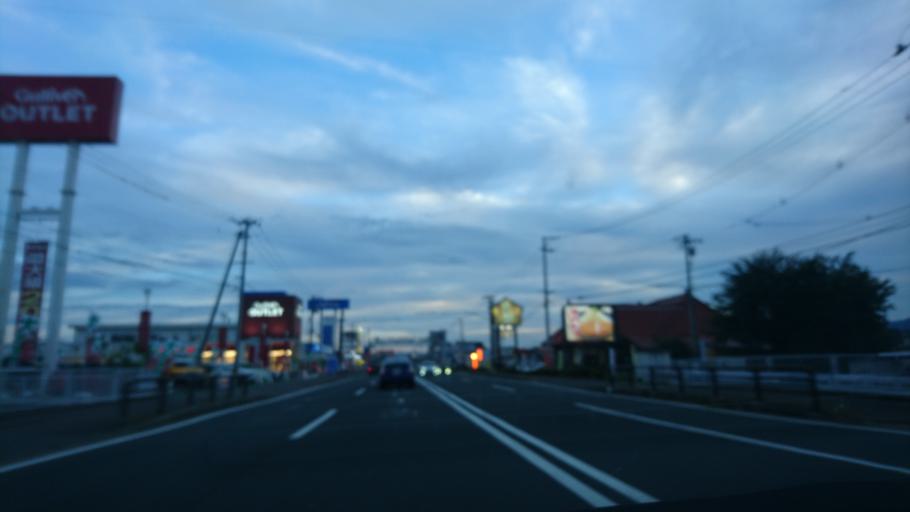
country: JP
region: Iwate
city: Morioka-shi
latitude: 39.6782
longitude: 141.1557
